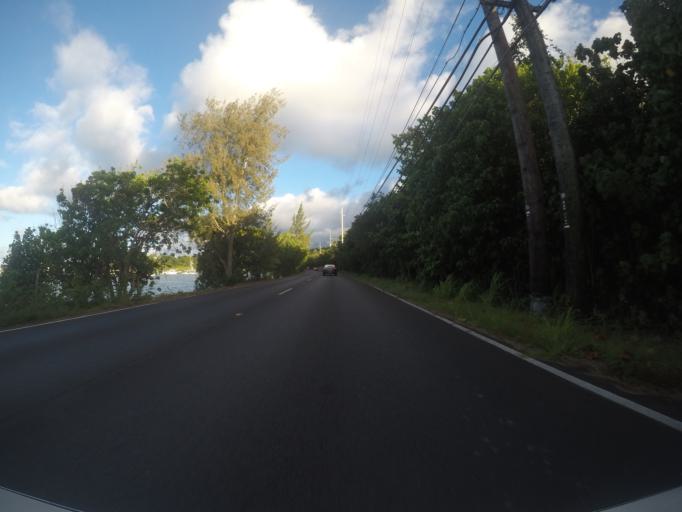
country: US
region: Hawaii
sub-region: Honolulu County
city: He'eia
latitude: 21.4448
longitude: -157.8130
